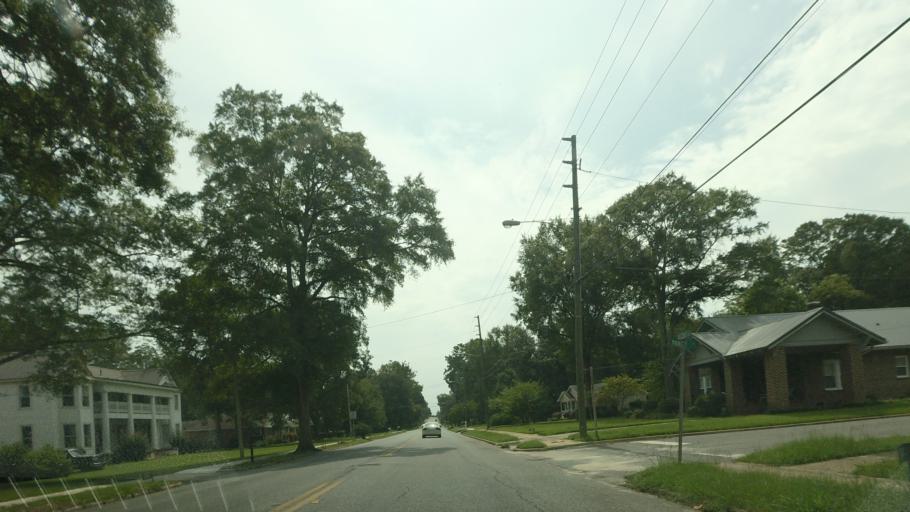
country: US
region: Georgia
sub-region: Bleckley County
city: Cochran
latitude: 32.3846
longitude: -83.3524
